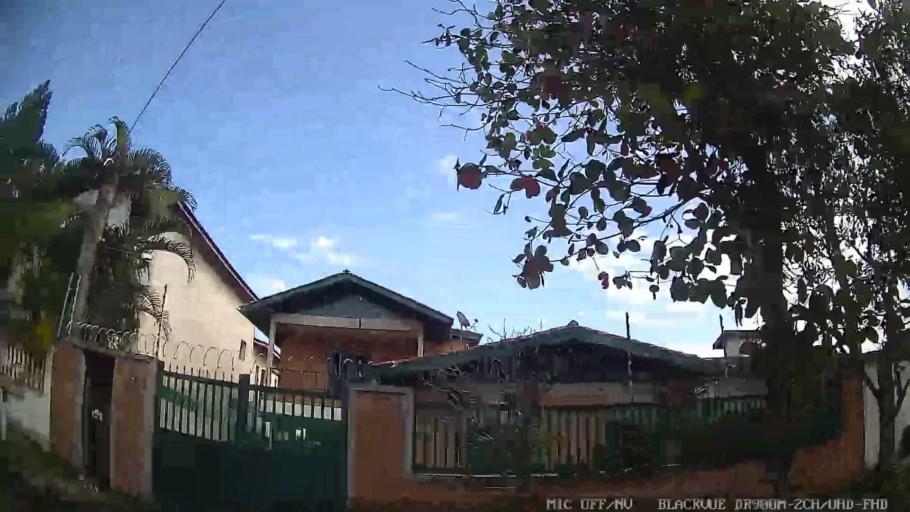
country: BR
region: Sao Paulo
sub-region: Guaruja
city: Guaruja
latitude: -23.9767
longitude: -46.2112
